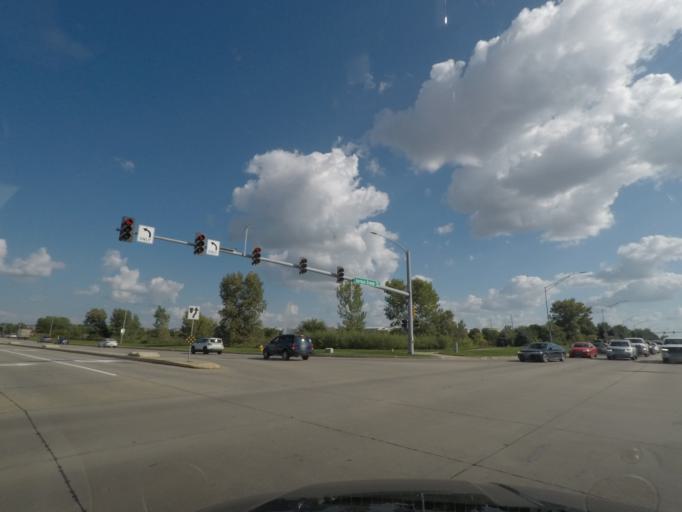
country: US
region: Iowa
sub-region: Dallas County
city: Waukee
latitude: 41.5734
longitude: -93.8092
